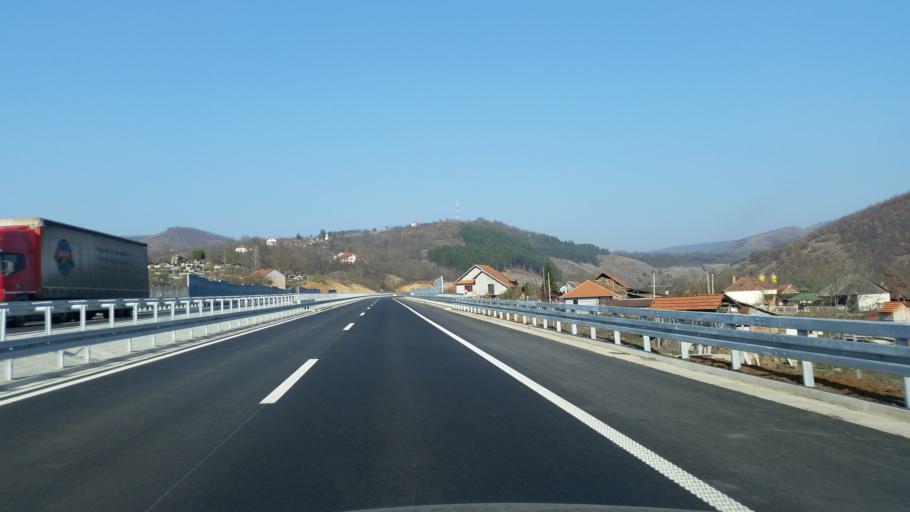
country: RS
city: Prislonica
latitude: 43.9667
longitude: 20.3960
